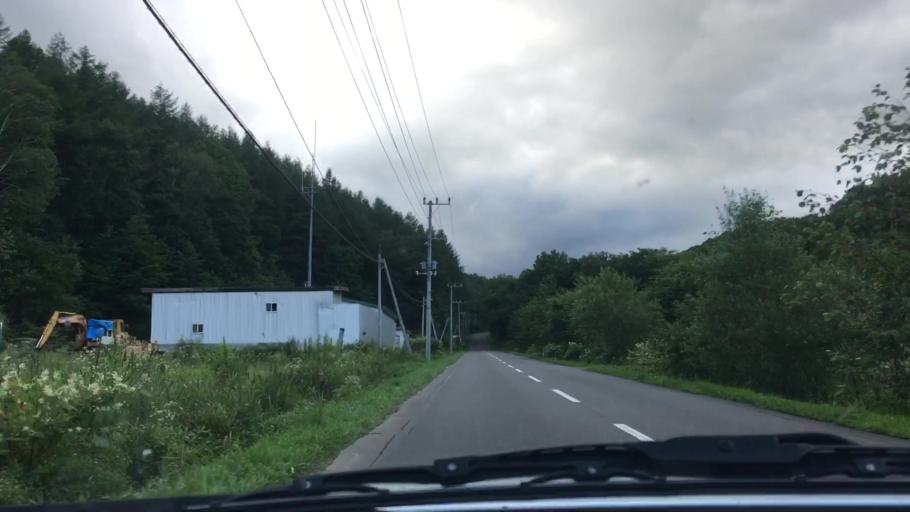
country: JP
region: Hokkaido
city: Otofuke
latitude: 43.1432
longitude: 142.8806
